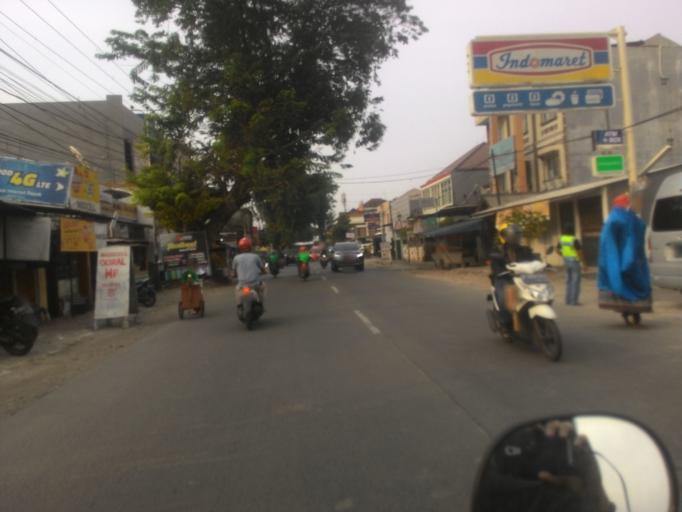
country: ID
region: West Java
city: Depok
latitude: -6.3947
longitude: 106.8368
